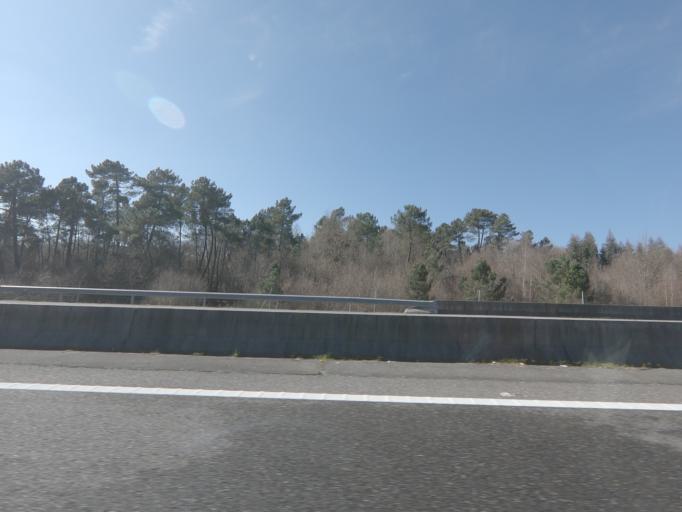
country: ES
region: Galicia
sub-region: Provincia de Ourense
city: Pinor
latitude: 42.4709
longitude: -8.0275
